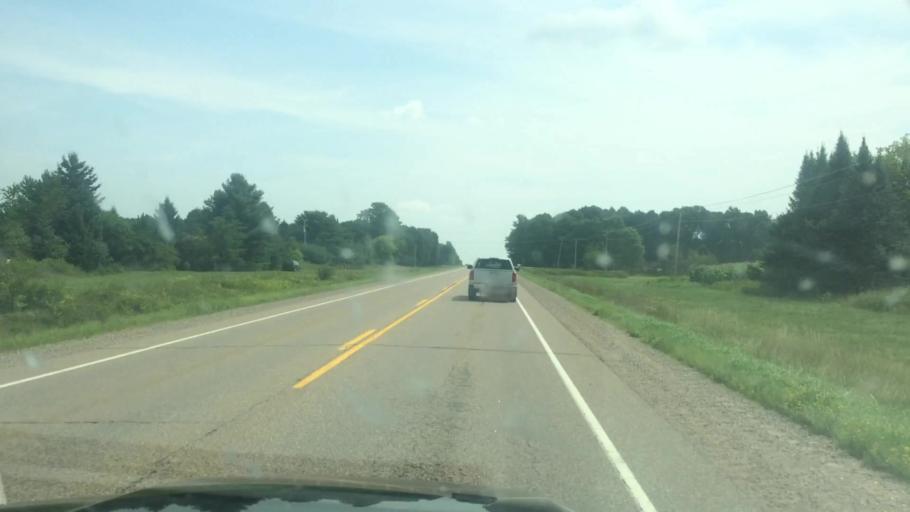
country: US
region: Wisconsin
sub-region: Langlade County
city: Antigo
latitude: 45.1681
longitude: -88.9005
